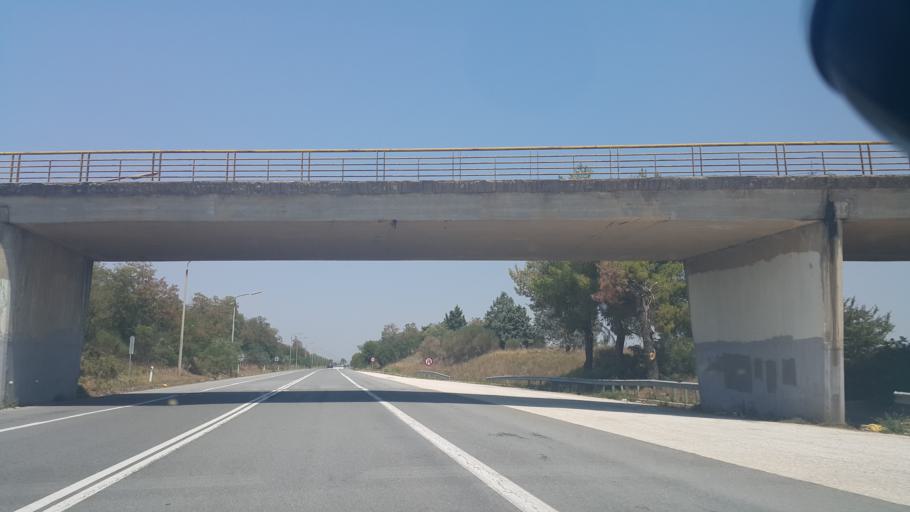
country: GR
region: Central Macedonia
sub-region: Nomos Thessalonikis
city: Prochoma
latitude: 40.8445
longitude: 22.6678
